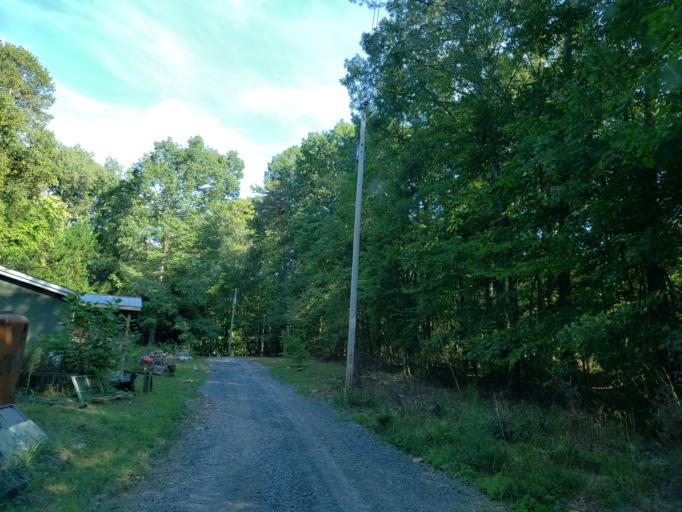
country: US
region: Georgia
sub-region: Fannin County
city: Blue Ridge
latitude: 34.6755
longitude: -84.2651
